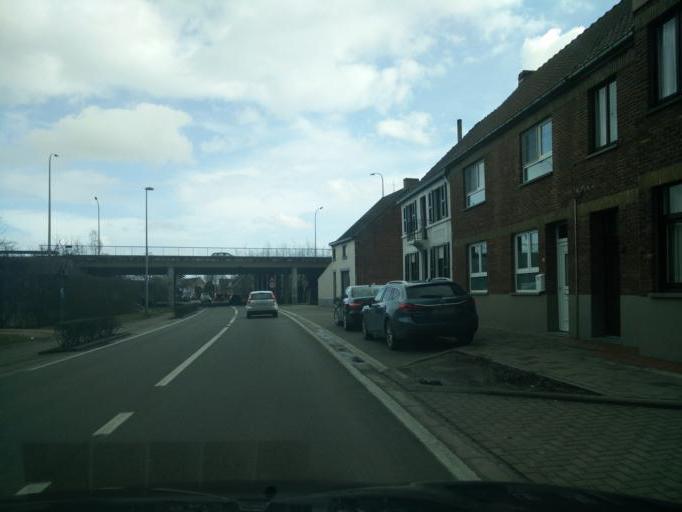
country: BE
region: Flanders
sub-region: Provincie Oost-Vlaanderen
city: Laarne
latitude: 51.0336
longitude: 3.8238
